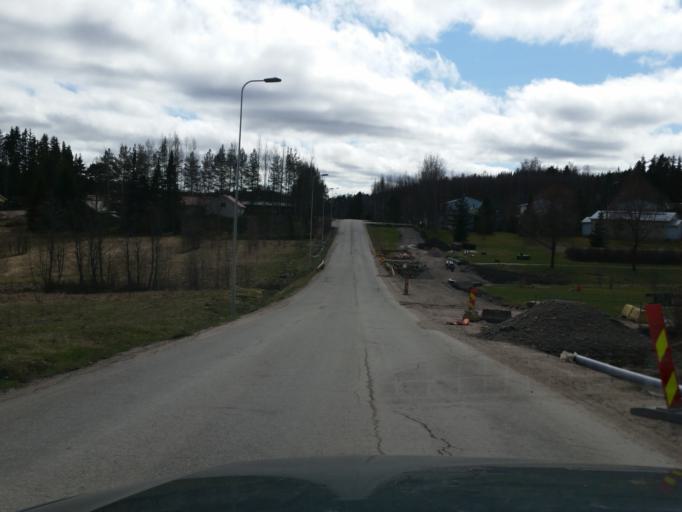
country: FI
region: Uusimaa
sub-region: Helsinki
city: Vihti
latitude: 60.4053
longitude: 24.3301
